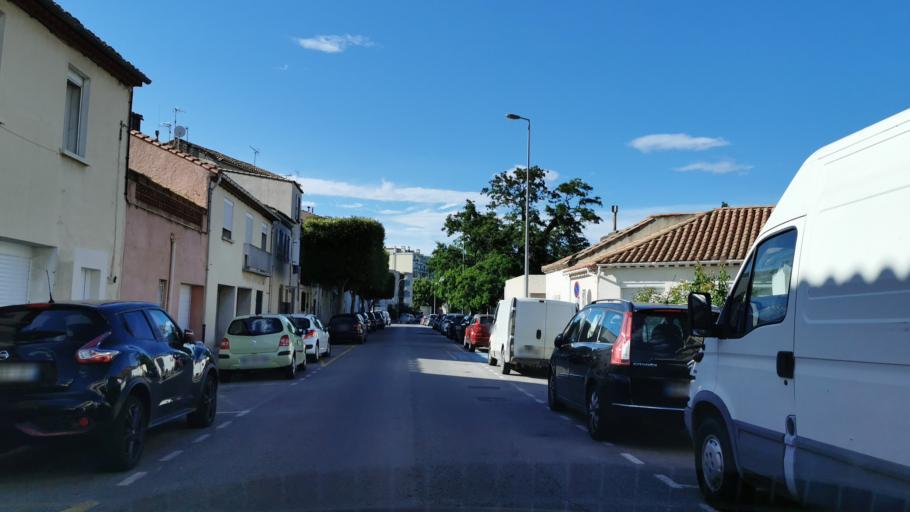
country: FR
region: Languedoc-Roussillon
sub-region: Departement de l'Aude
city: Narbonne
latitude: 43.1893
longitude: 3.0095
